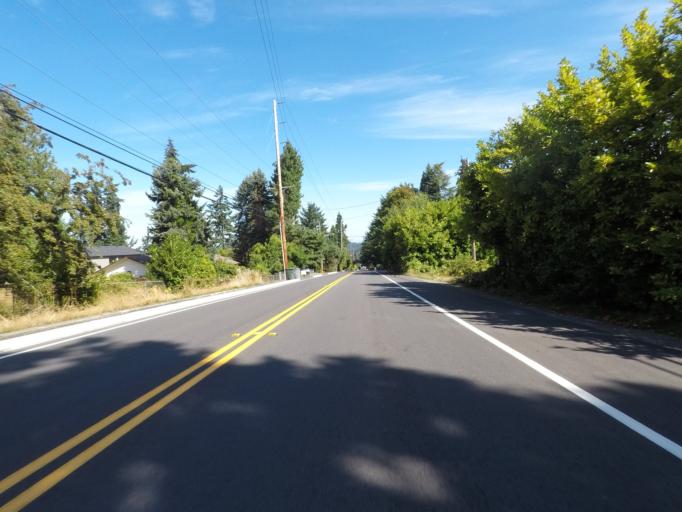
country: US
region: Washington
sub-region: King County
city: Kenmore
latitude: 47.7420
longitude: -122.2289
